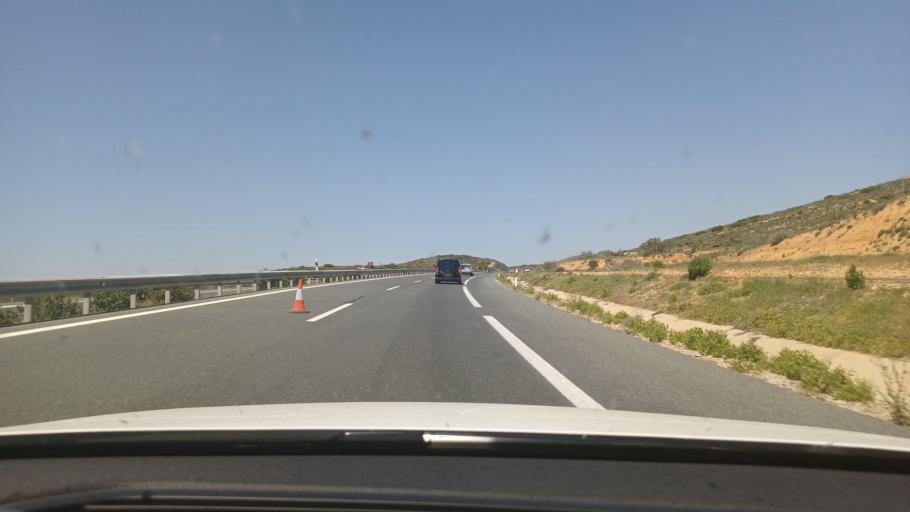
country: ES
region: Castille-La Mancha
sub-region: Provincia de Albacete
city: Almansa
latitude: 38.8755
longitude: -1.1817
